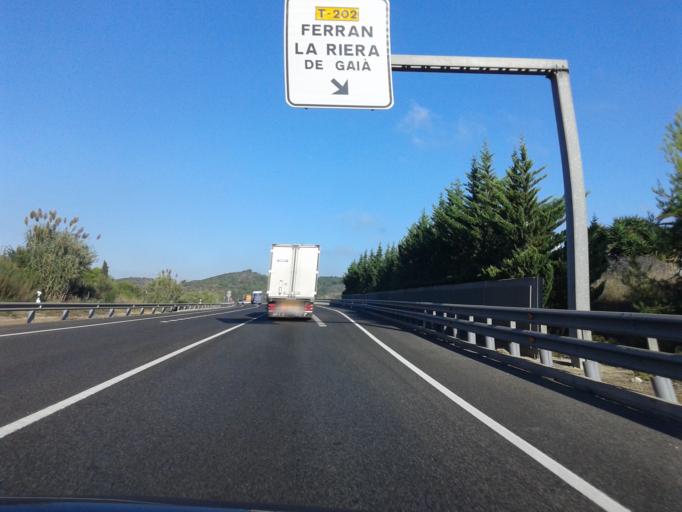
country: ES
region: Catalonia
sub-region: Provincia de Tarragona
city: Altafulla
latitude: 41.1470
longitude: 1.3560
